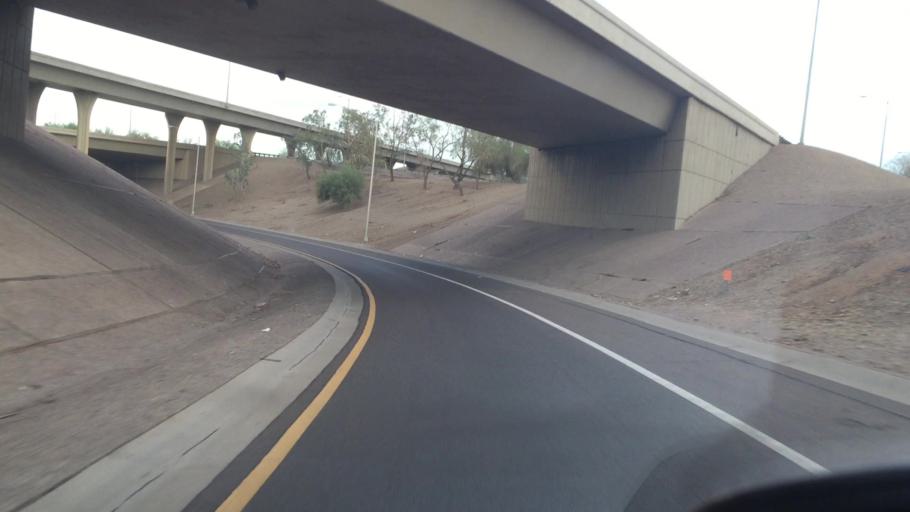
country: US
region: Arizona
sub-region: Maricopa County
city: Phoenix
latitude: 33.4269
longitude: -112.0382
